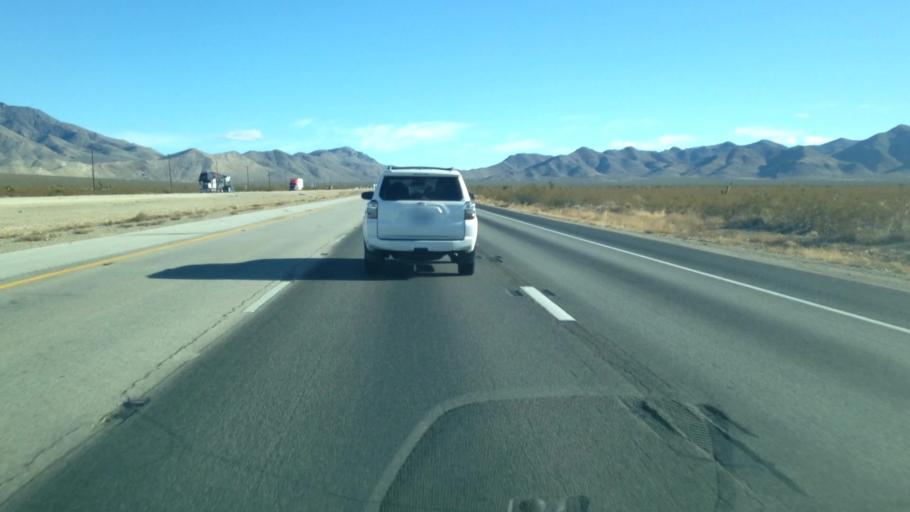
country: US
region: Nevada
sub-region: Clark County
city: Sandy Valley
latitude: 35.4482
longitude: -115.6617
